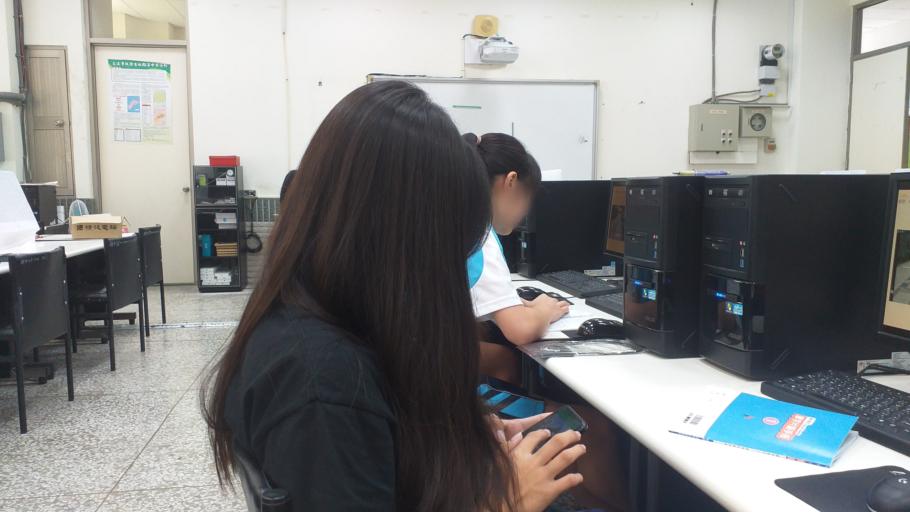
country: TW
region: Taiwan
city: Xinying
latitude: 23.3084
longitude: 120.3113
